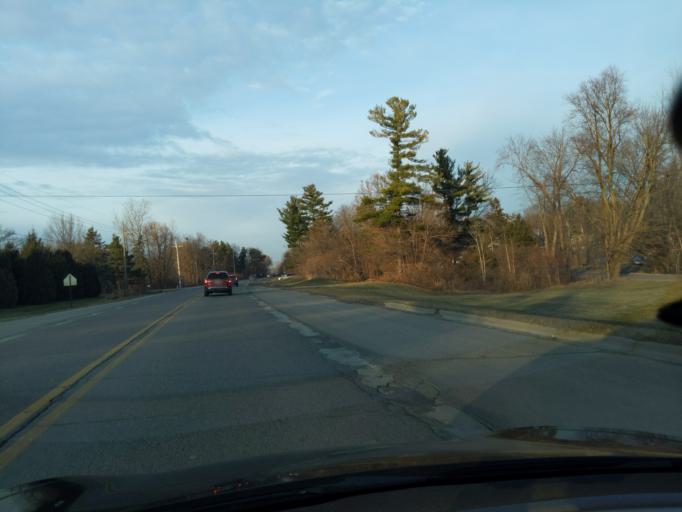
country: US
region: Michigan
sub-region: Livingston County
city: Brighton
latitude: 42.5616
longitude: -83.7550
